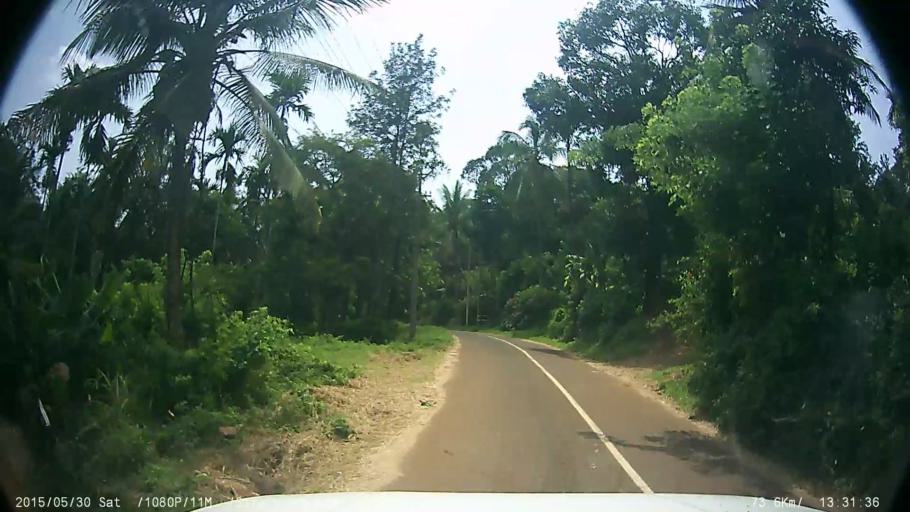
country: IN
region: Kerala
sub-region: Wayanad
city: Panamaram
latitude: 11.8162
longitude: 76.0831
